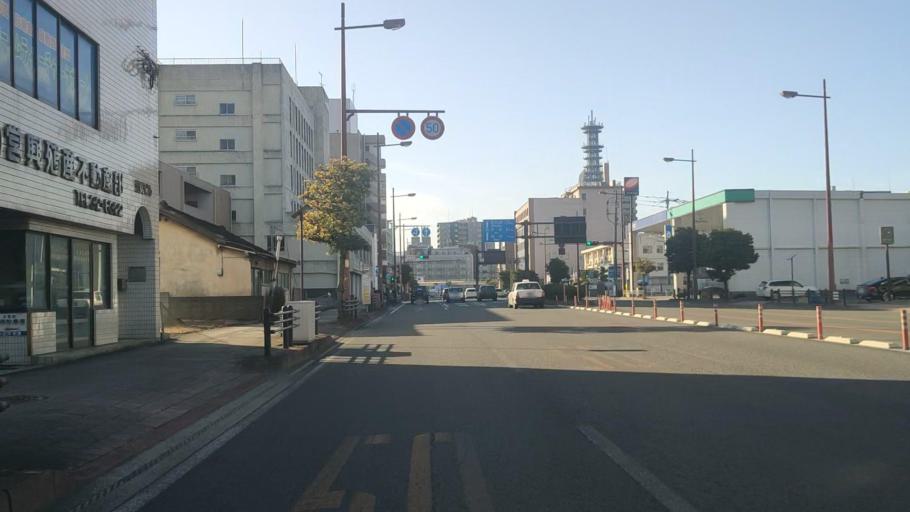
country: JP
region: Oita
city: Oita
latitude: 33.2320
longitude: 131.6156
